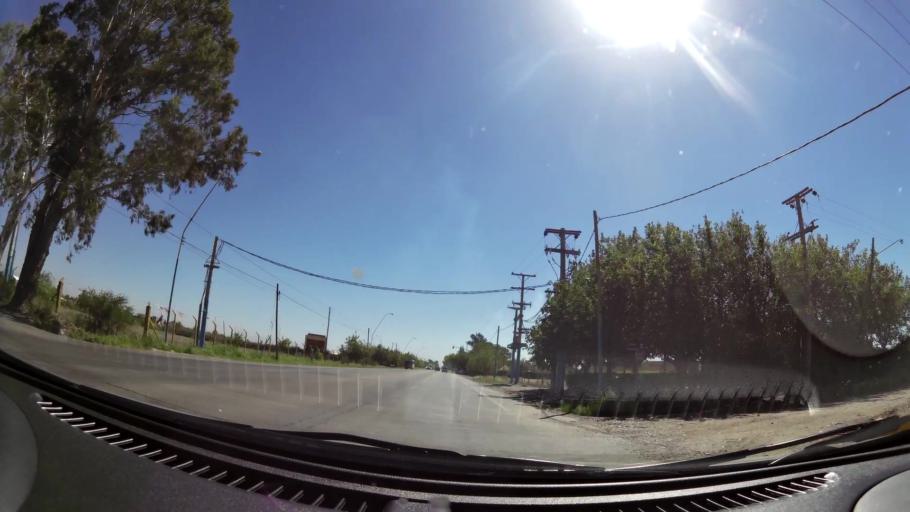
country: AR
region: San Juan
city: Villa Aberastain
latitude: -31.6244
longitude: -68.5520
